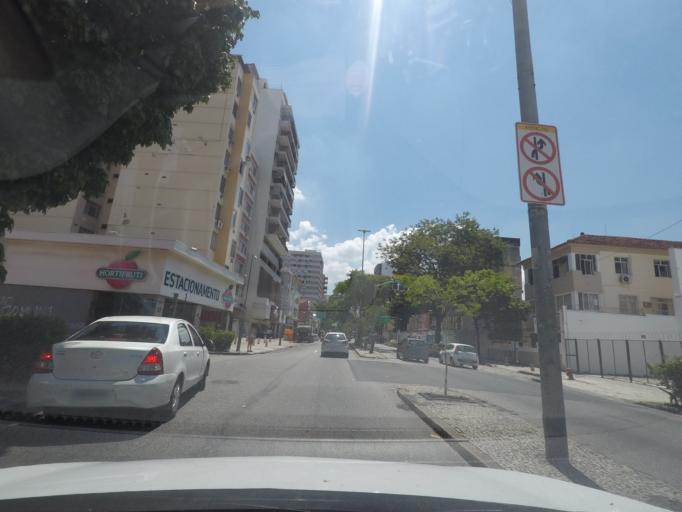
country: BR
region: Rio de Janeiro
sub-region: Rio De Janeiro
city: Rio de Janeiro
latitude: -22.9149
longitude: -43.2405
